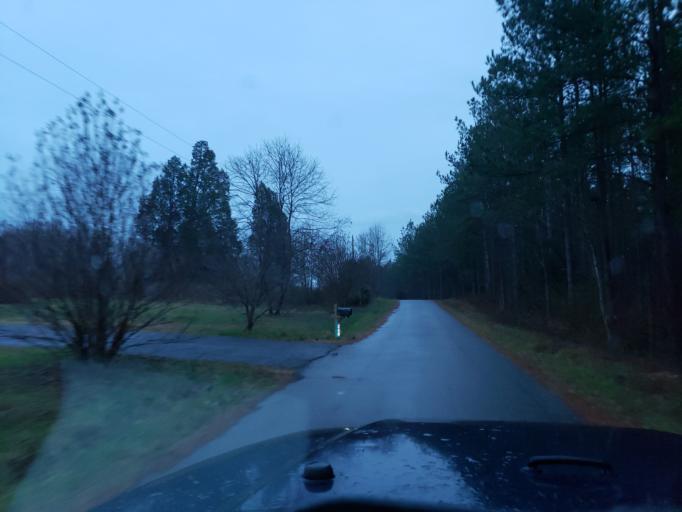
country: US
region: North Carolina
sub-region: Cleveland County
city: White Plains
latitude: 35.1487
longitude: -81.4245
